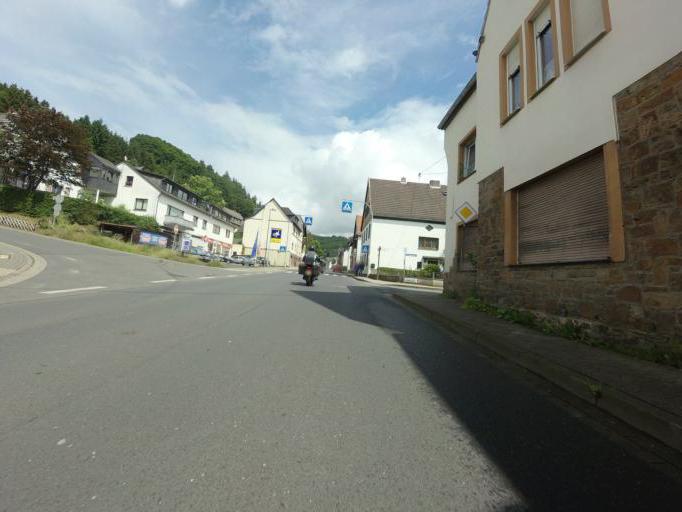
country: DE
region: Rheinland-Pfalz
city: Adenau
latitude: 50.3817
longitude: 6.9379
